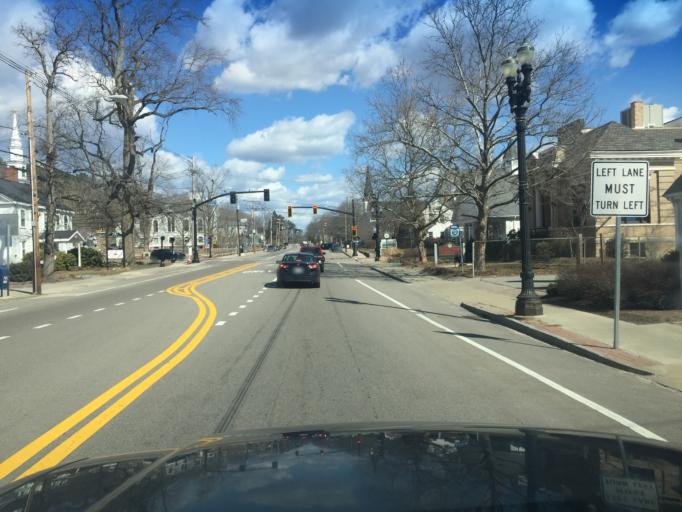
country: US
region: Massachusetts
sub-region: Middlesex County
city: Holliston
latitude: 42.2001
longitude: -71.4297
